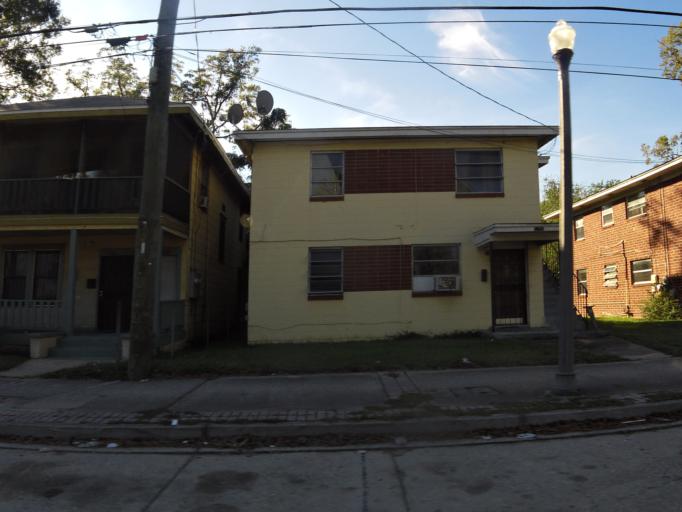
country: US
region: Florida
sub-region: Duval County
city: Jacksonville
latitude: 30.3469
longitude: -81.6758
